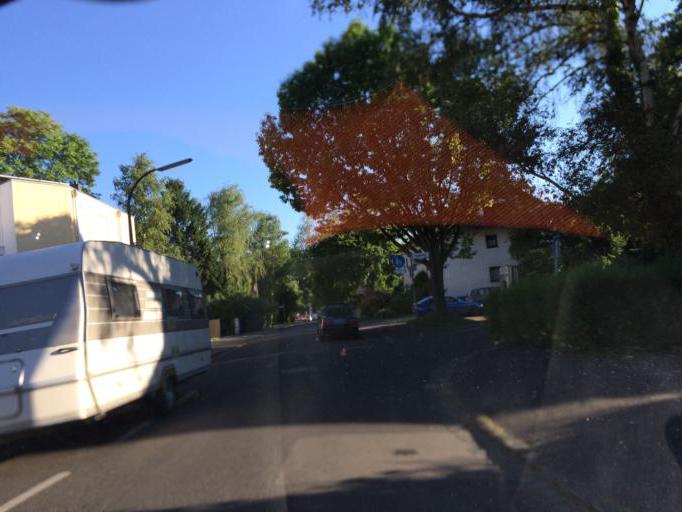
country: DE
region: North Rhine-Westphalia
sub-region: Regierungsbezirk Koln
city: Konigswinter
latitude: 50.6792
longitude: 7.1713
